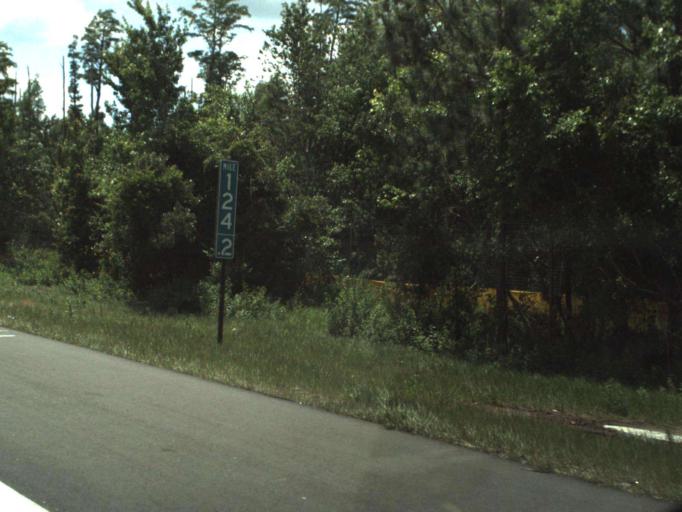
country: US
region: Florida
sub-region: Volusia County
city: Samsula-Spruce Creek
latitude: 29.0826
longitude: -81.1705
